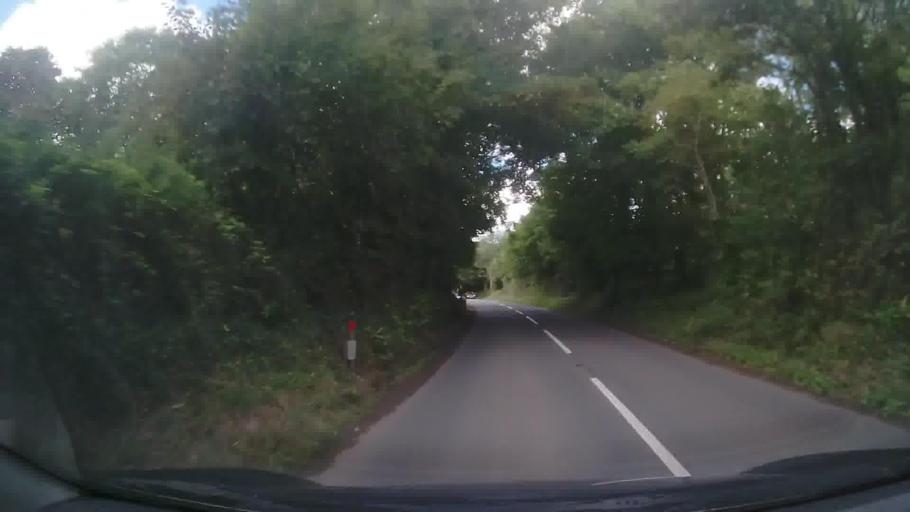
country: GB
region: Wales
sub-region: Pembrokeshire
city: Manorbier
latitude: 51.6509
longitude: -4.7821
